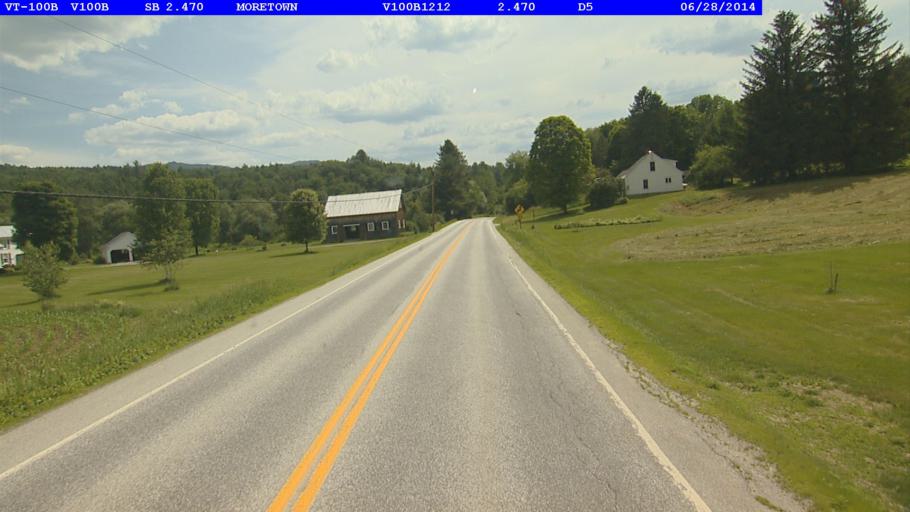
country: US
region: Vermont
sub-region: Washington County
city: Waterbury
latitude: 44.2649
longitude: -72.7471
